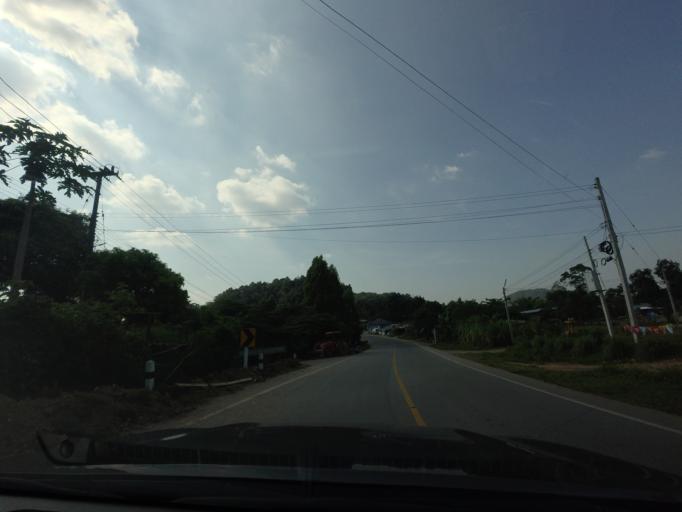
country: TH
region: Nan
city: Santi Suk
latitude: 18.9168
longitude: 100.8775
